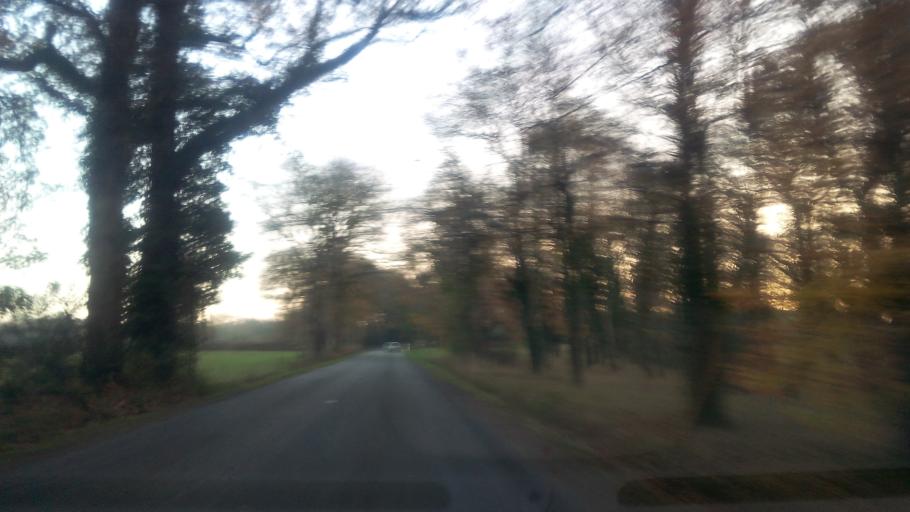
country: FR
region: Brittany
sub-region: Departement d'Ille-et-Vilaine
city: Bains-sur-Oust
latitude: 47.7142
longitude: -2.0539
